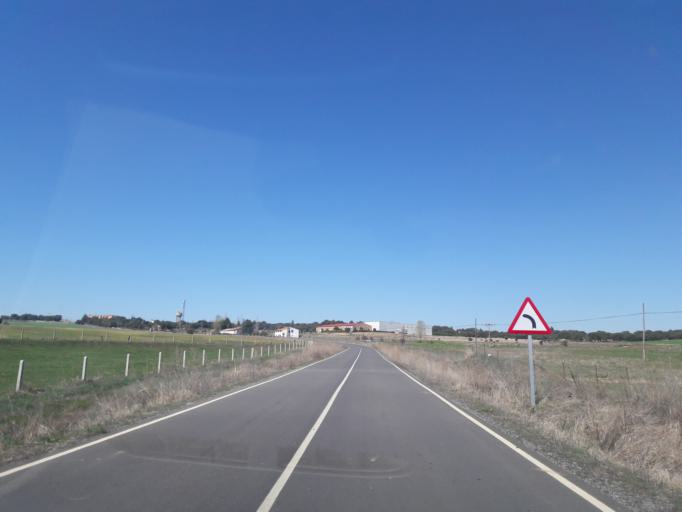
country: ES
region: Castille and Leon
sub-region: Provincia de Salamanca
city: Martinamor
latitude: 40.8098
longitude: -5.6214
